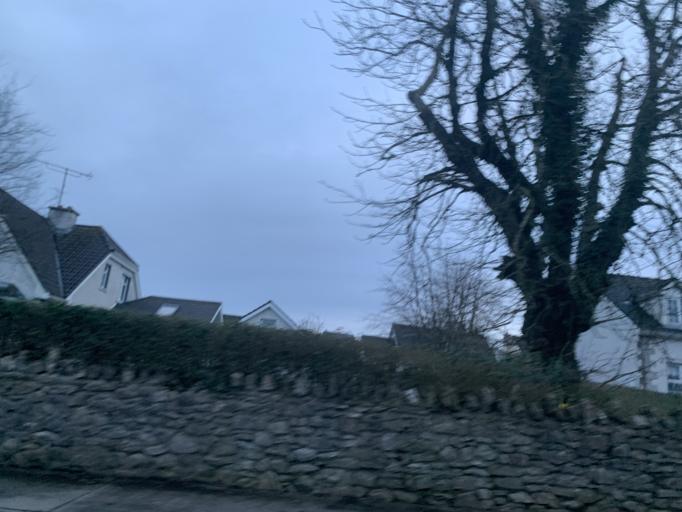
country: IE
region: Connaught
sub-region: Sligo
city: Collooney
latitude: 54.1834
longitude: -8.4889
